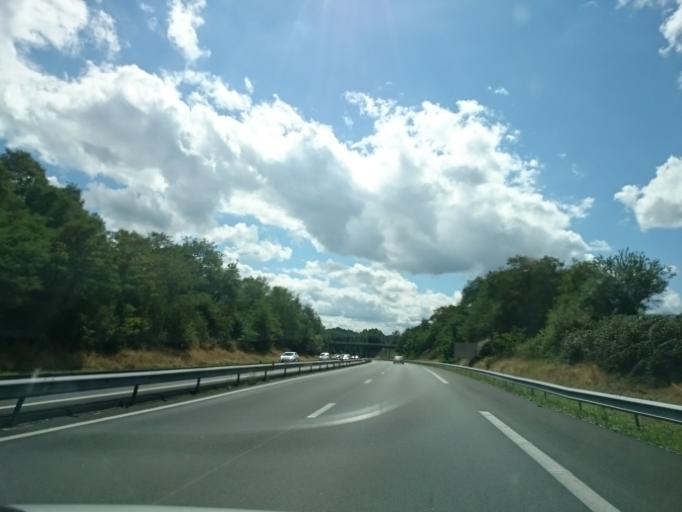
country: FR
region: Pays de la Loire
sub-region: Departement de Maine-et-Loire
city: Seiches-sur-le-Loir
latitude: 47.5825
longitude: -0.3322
